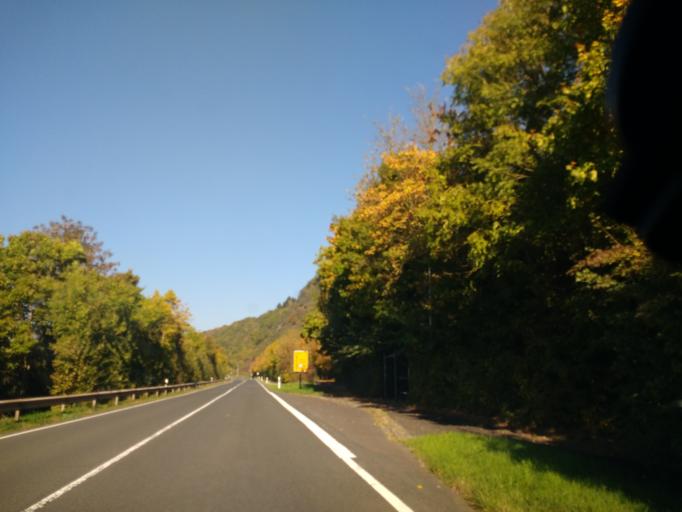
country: DE
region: Rheinland-Pfalz
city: Kanzem
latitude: 49.6746
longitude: 6.5623
